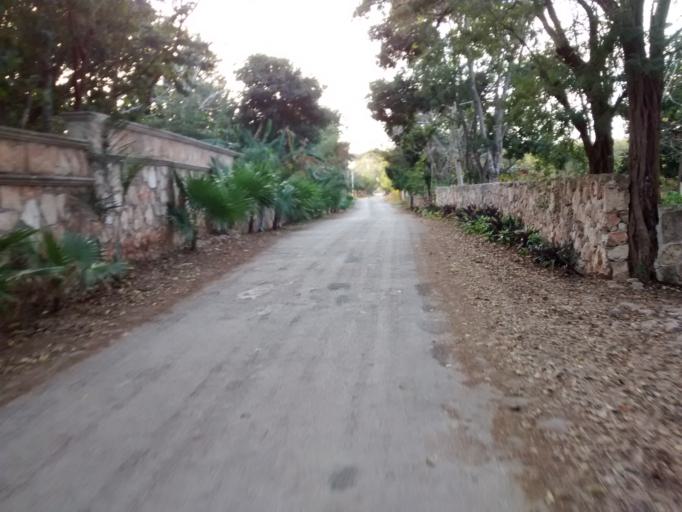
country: MX
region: Yucatan
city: Valladolid
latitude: 20.6806
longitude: -88.1609
